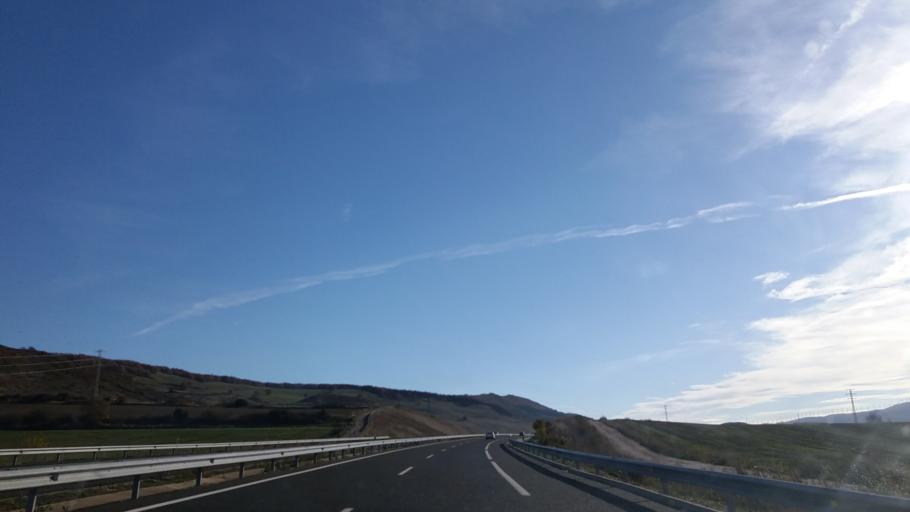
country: ES
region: Navarre
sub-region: Provincia de Navarra
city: Monreal
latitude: 42.7125
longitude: -1.5109
